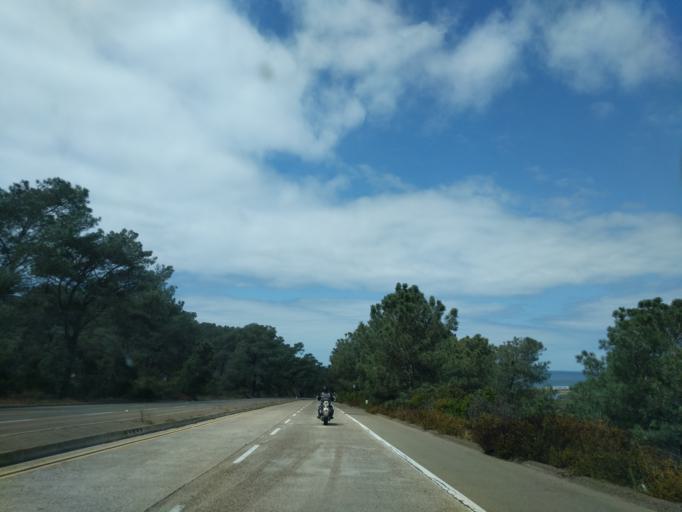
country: US
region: California
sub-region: San Diego County
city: Del Mar
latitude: 32.9235
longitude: -117.2525
